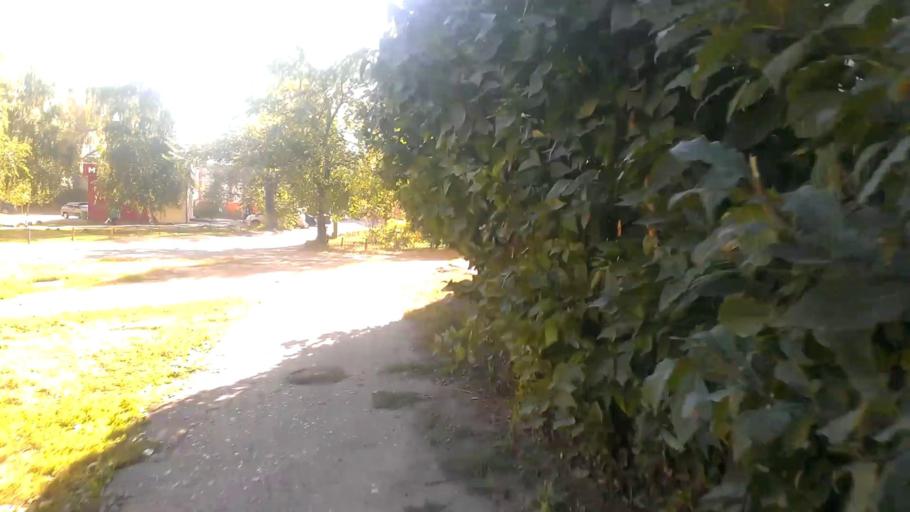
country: RU
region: Altai Krai
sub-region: Gorod Barnaulskiy
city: Barnaul
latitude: 53.3725
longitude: 83.6911
